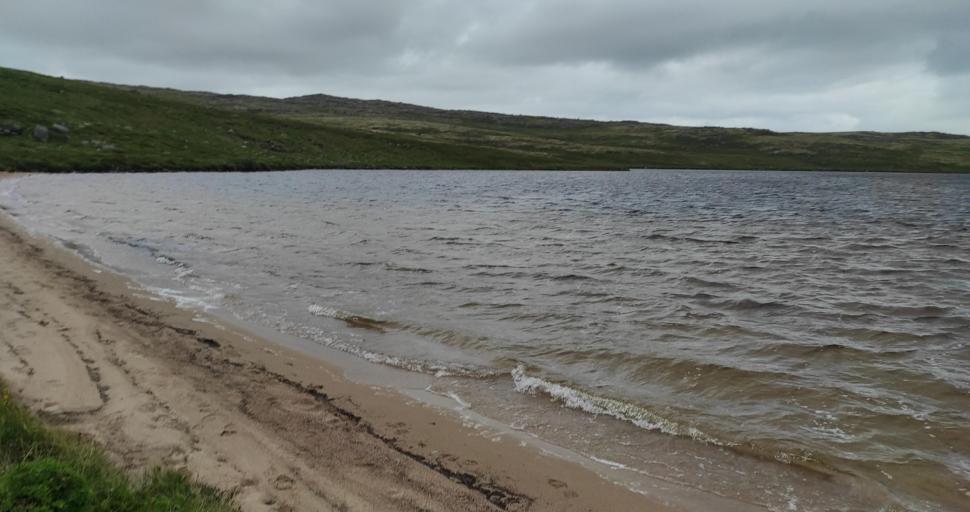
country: RU
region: Murmansk
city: Teriberka
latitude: 69.2121
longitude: 35.4591
